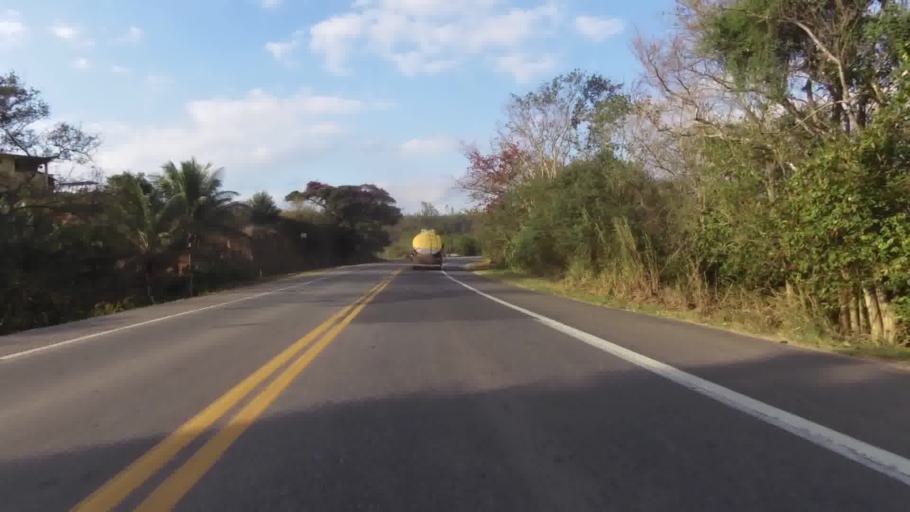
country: BR
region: Espirito Santo
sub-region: Cachoeiro De Itapemirim
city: Cachoeiro de Itapemirim
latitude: -20.9010
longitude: -41.0575
